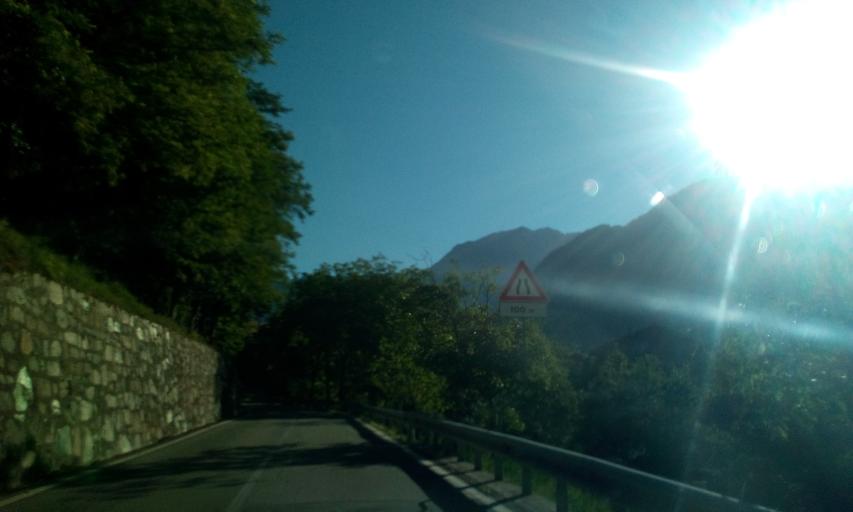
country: IT
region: Aosta Valley
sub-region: Valle d'Aosta
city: Challand-Saint-Anselme
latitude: 45.7014
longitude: 7.7249
